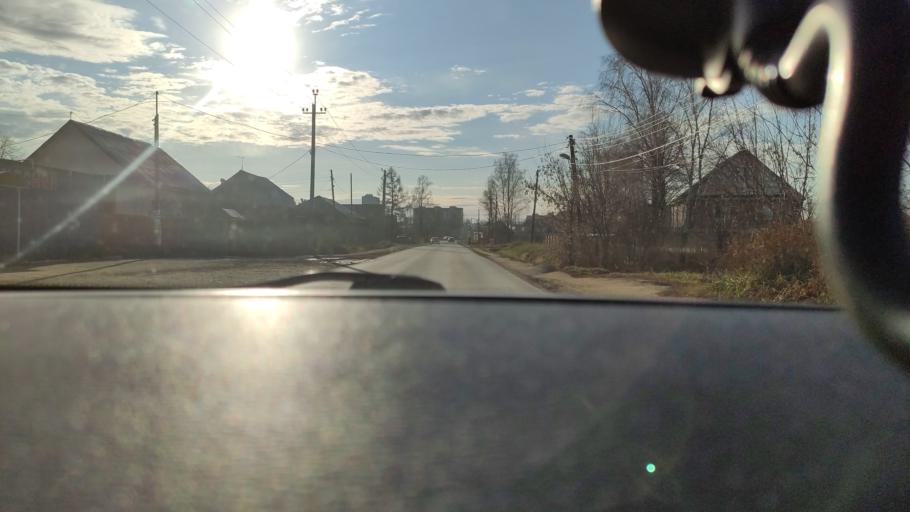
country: RU
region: Perm
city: Kondratovo
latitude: 58.0489
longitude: 56.0303
